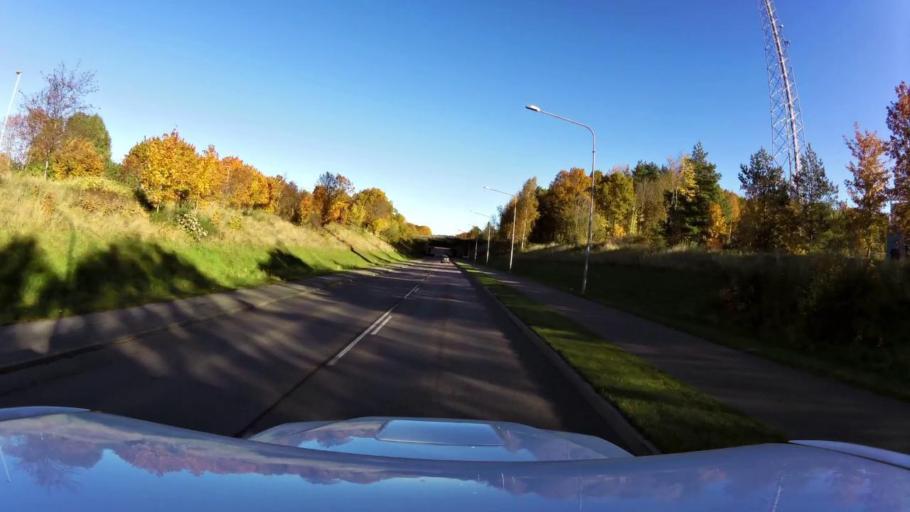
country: SE
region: OEstergoetland
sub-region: Linkopings Kommun
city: Ljungsbro
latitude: 58.4999
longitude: 15.5052
